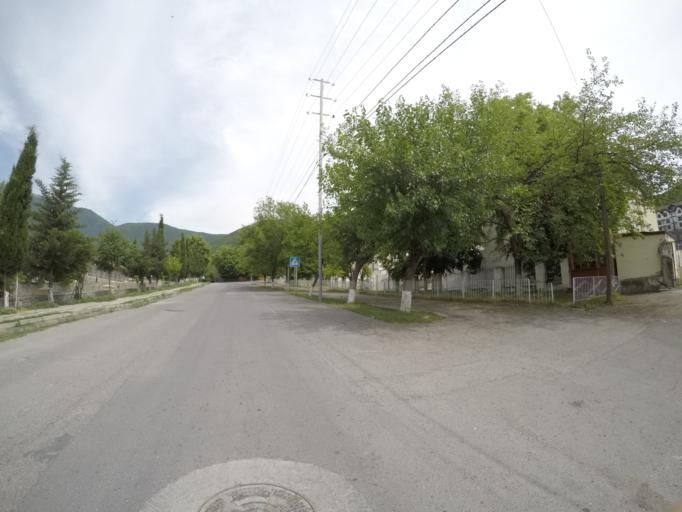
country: AZ
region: Shaki City
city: Sheki
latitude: 41.2001
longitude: 47.1873
